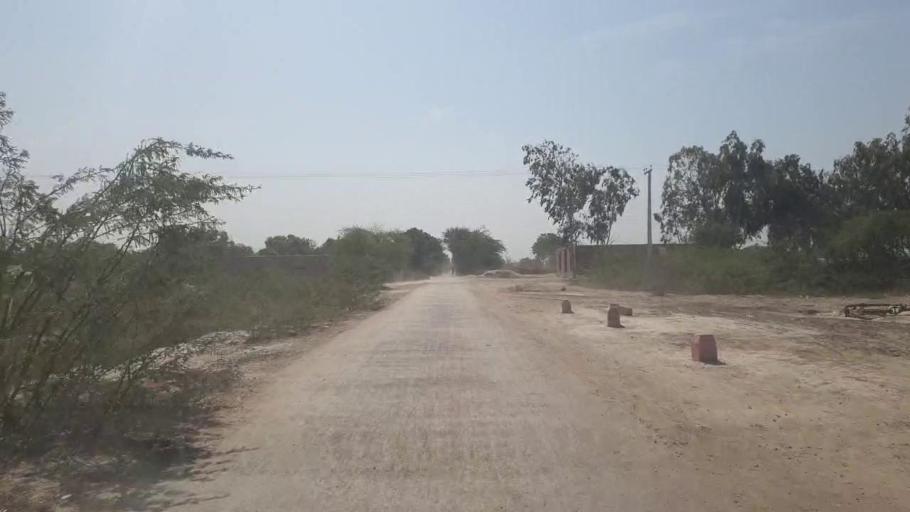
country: PK
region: Sindh
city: Kunri
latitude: 25.2593
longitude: 69.5782
